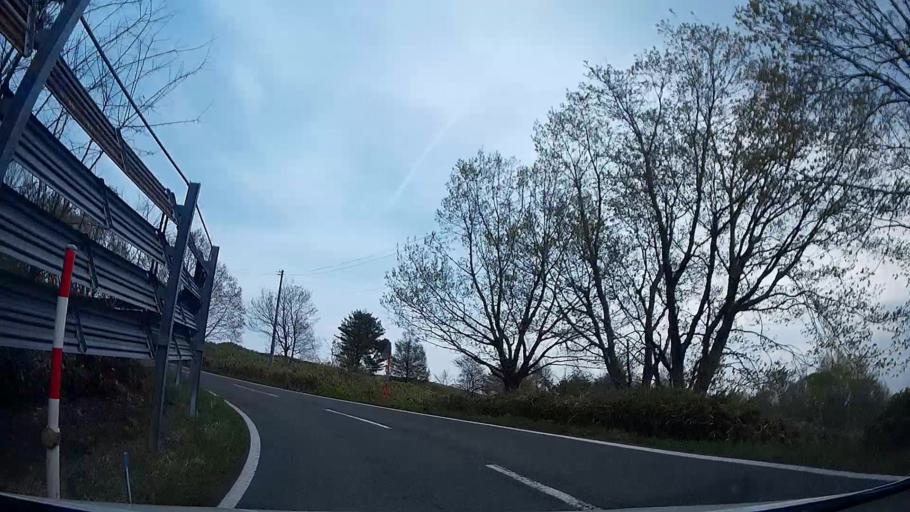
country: JP
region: Iwate
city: Shizukuishi
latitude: 39.9251
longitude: 140.9774
